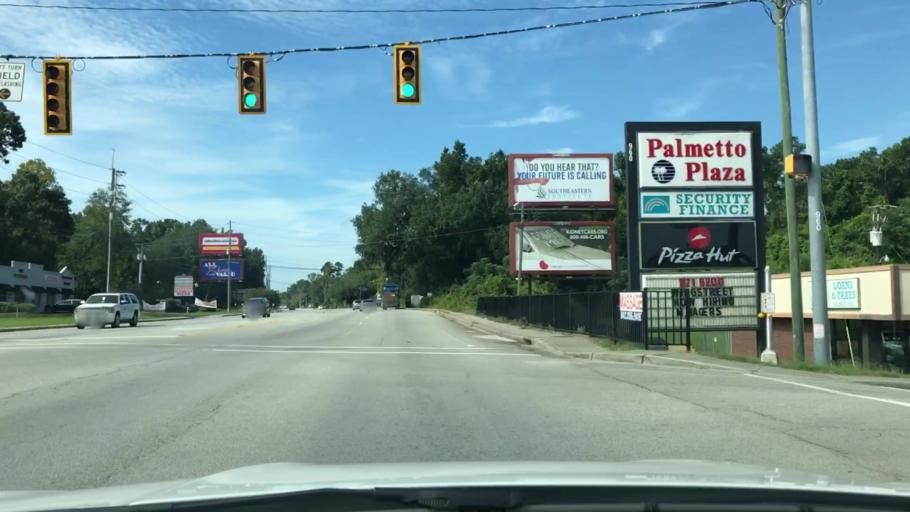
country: US
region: South Carolina
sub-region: Dorchester County
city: Centerville
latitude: 32.9958
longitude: -80.1866
